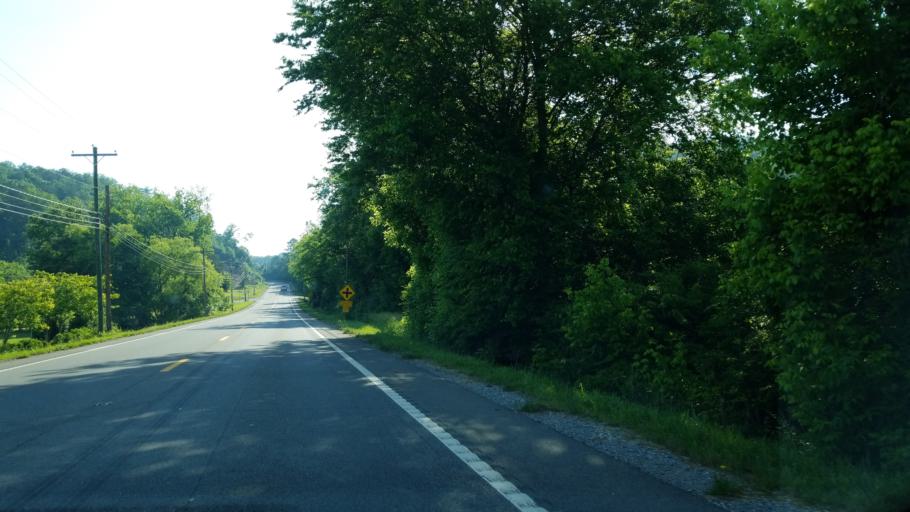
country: US
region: Tennessee
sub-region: Hamilton County
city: Collegedale
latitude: 35.0879
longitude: -85.0144
